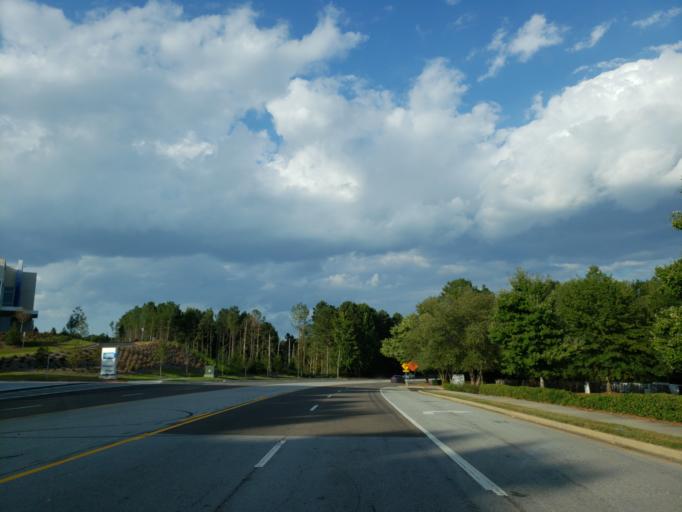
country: US
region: Georgia
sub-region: Cobb County
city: Mableton
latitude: 33.7613
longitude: -84.5656
